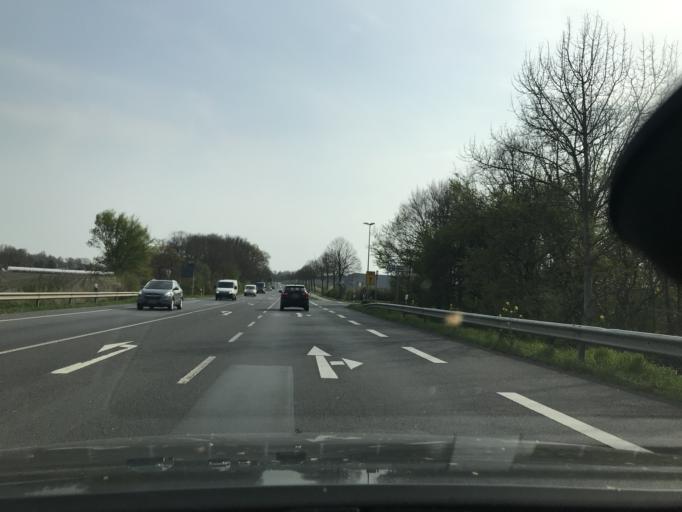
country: DE
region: North Rhine-Westphalia
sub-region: Regierungsbezirk Dusseldorf
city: Kevelaer
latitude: 51.5682
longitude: 6.2641
